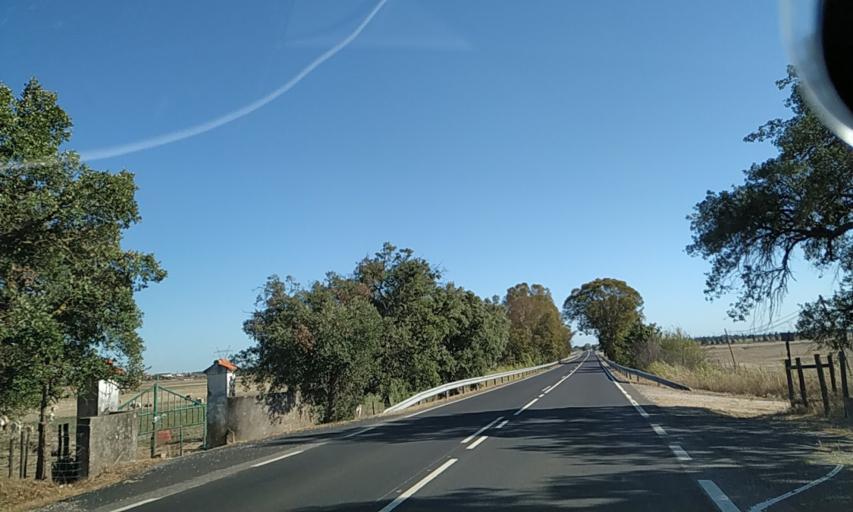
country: PT
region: Santarem
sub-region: Benavente
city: Samora Correia
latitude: 38.8908
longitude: -8.8814
